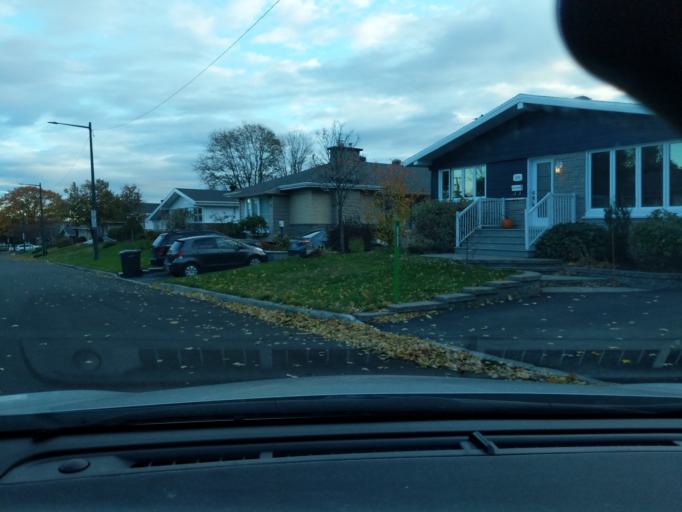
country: CA
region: Quebec
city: L'Ancienne-Lorette
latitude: 46.7651
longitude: -71.2838
